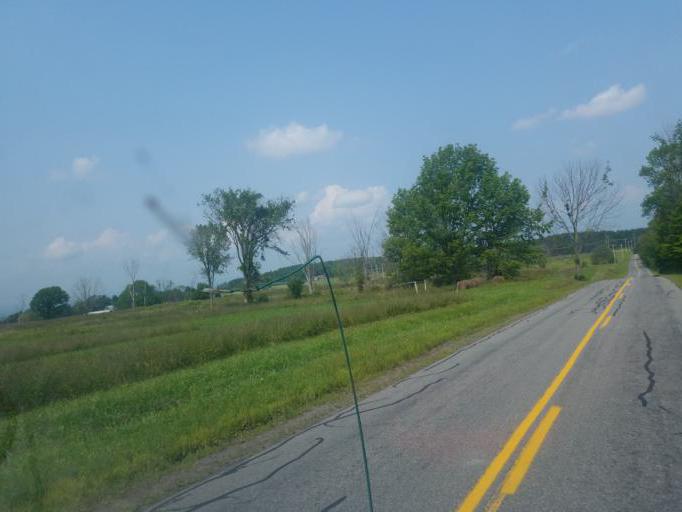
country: US
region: New York
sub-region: Montgomery County
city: Fonda
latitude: 42.8574
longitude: -74.3693
